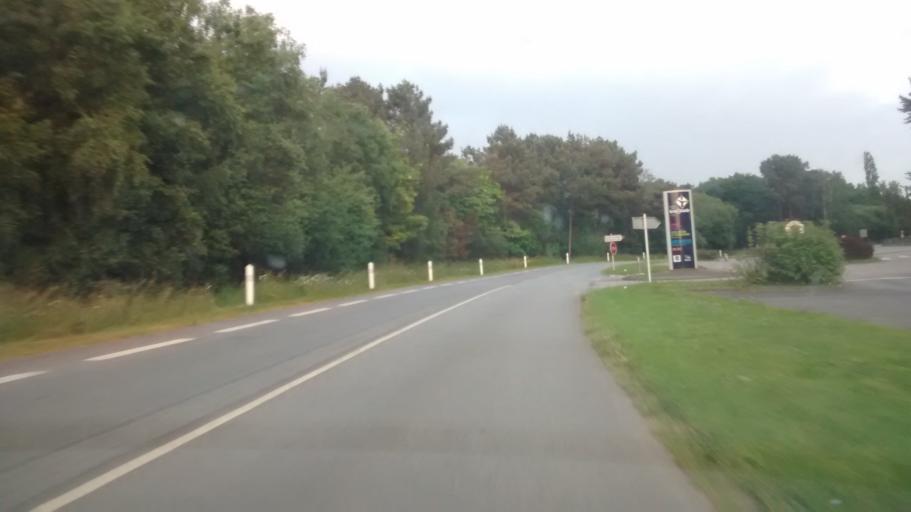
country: FR
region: Brittany
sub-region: Departement du Morbihan
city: Beignon
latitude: 47.9522
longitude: -2.1364
